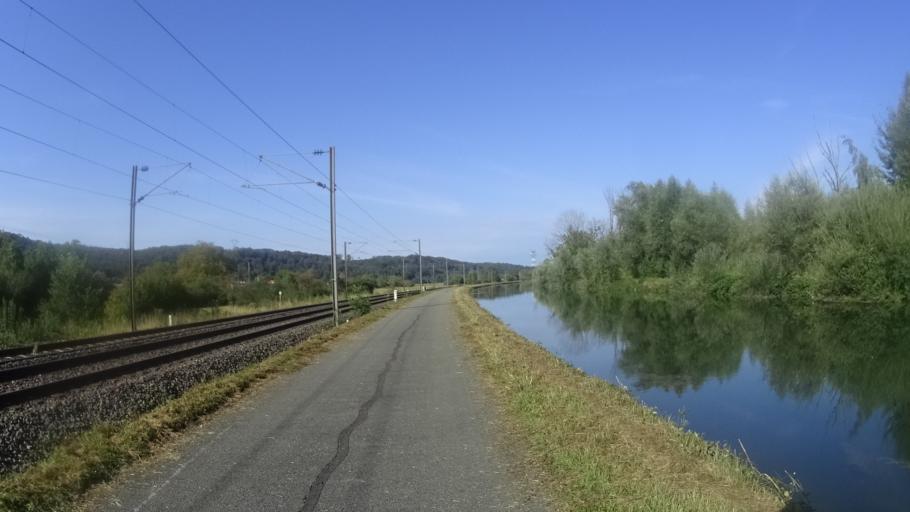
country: FR
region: Franche-Comte
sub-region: Departement du Doubs
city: Colombier-Fontaine
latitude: 47.4508
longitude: 6.6819
